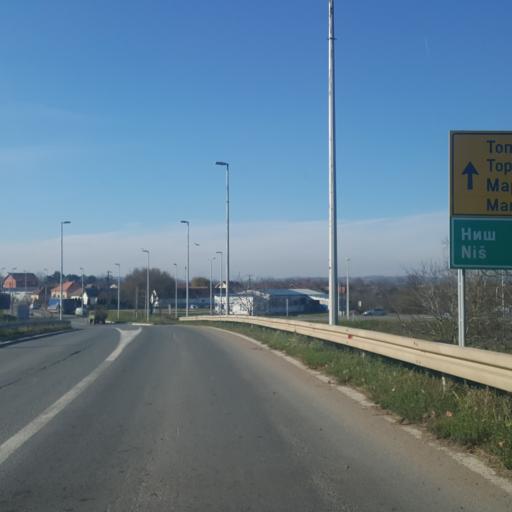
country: RS
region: Central Serbia
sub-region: Sumadijski Okrug
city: Lapovo
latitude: 44.2386
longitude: 21.1179
